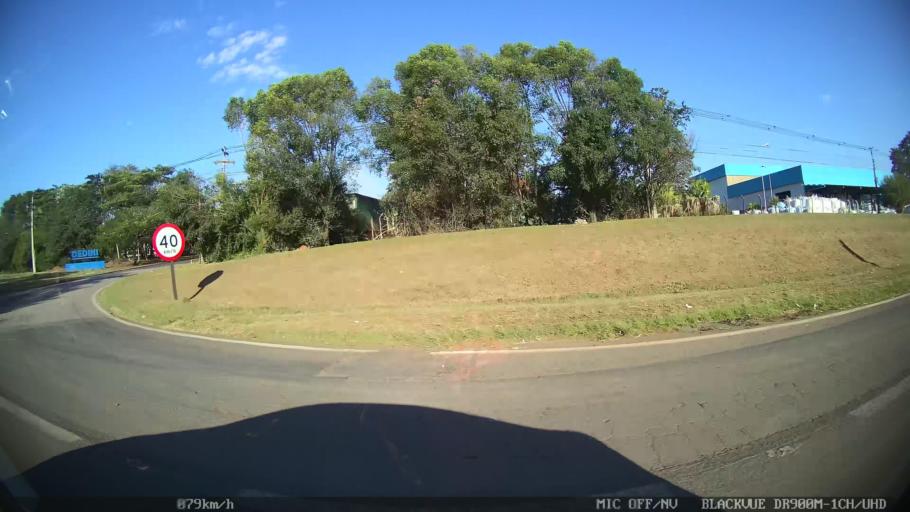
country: BR
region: Sao Paulo
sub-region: Piracicaba
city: Piracicaba
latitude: -22.6693
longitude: -47.6249
